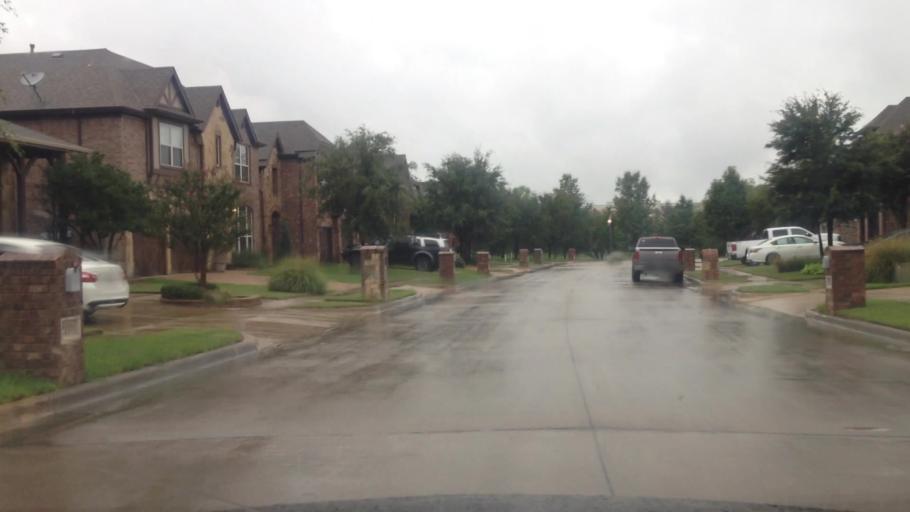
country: US
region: Texas
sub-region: Tarrant County
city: Watauga
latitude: 32.8945
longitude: -97.2411
